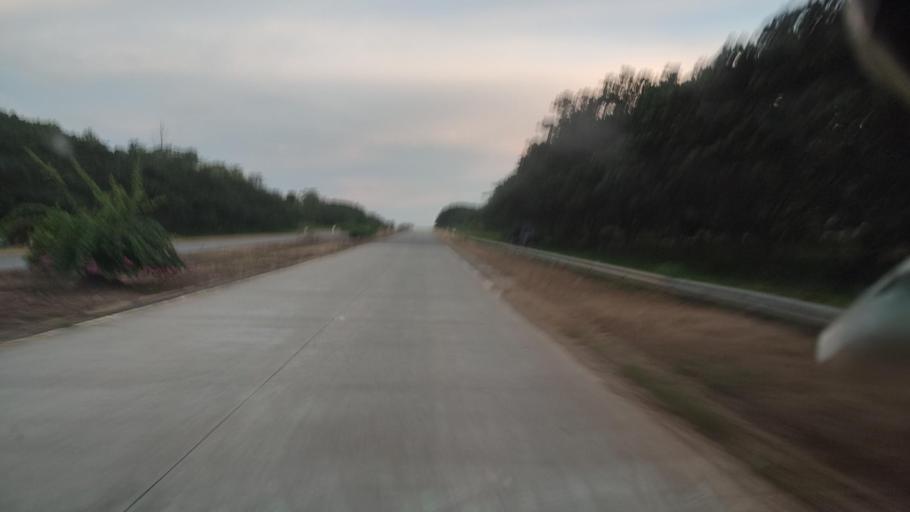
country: MM
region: Mandalay
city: Yamethin
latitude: 20.2572
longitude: 95.8921
